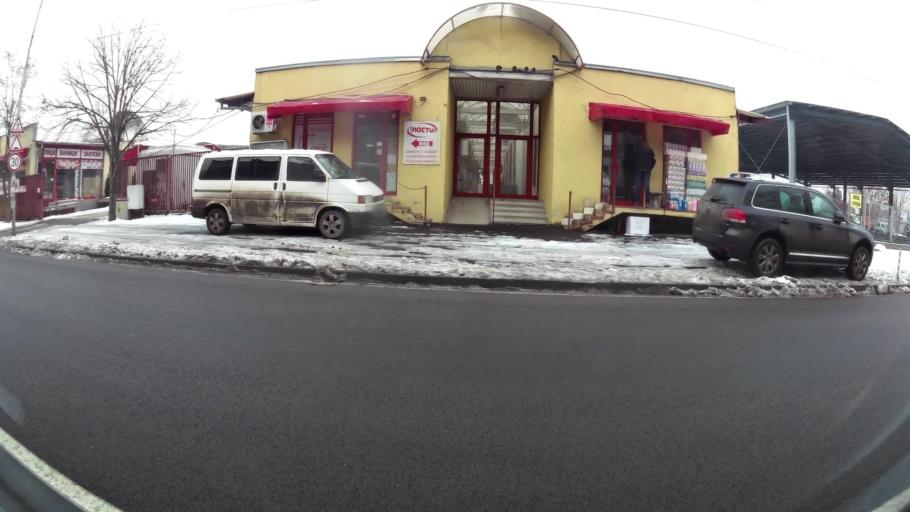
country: BG
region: Sofia-Capital
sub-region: Stolichna Obshtina
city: Sofia
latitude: 42.7101
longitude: 23.3464
